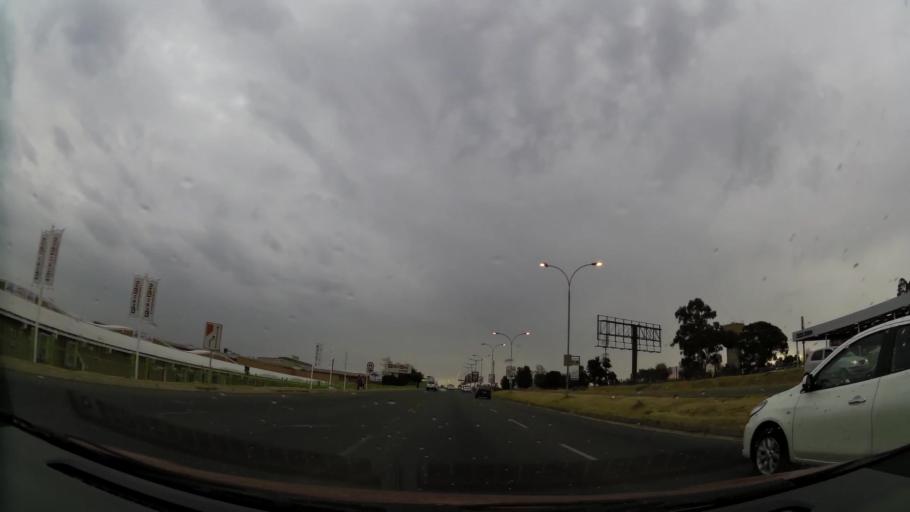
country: ZA
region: Gauteng
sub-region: City of Johannesburg Metropolitan Municipality
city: Roodepoort
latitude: -26.1295
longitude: 27.8507
